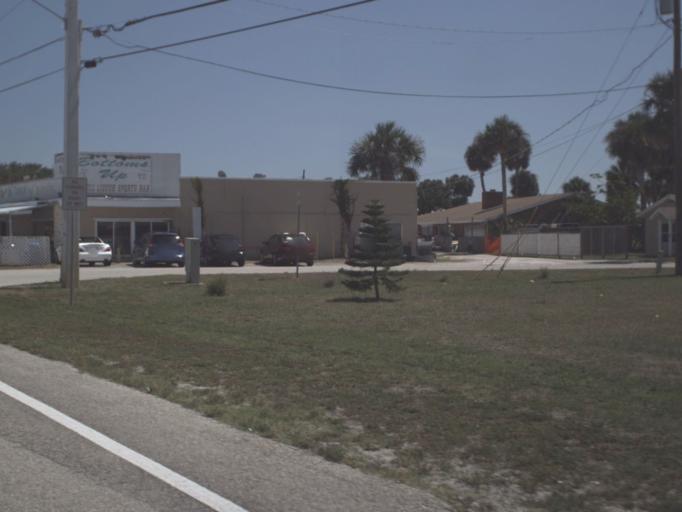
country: US
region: Florida
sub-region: Brevard County
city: Micco
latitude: 27.8754
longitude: -80.4987
